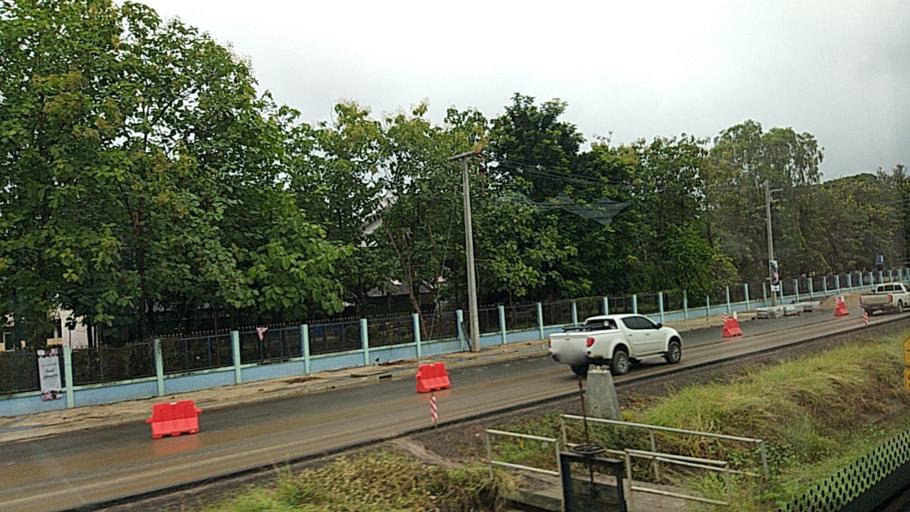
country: TH
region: Nakhon Ratchasima
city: Nakhon Ratchasima
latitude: 14.9951
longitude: 102.0722
